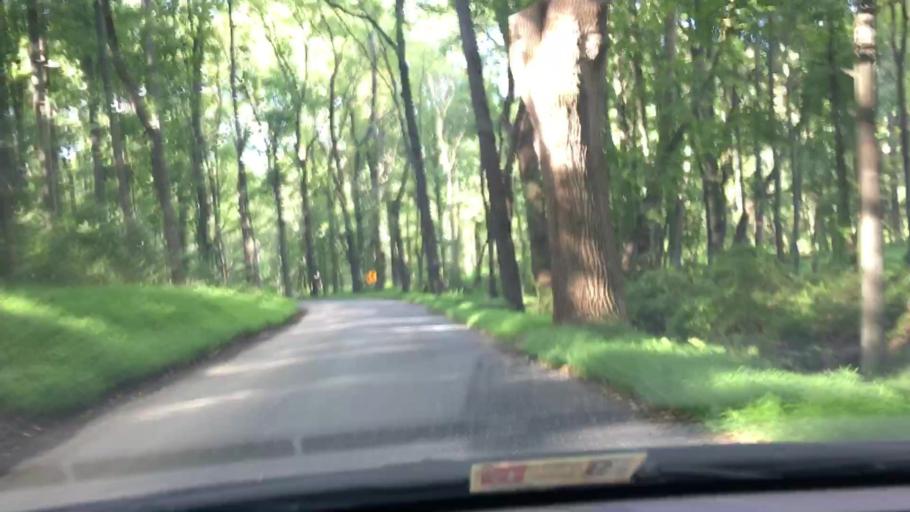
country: US
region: Maryland
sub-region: Montgomery County
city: Montgomery Village
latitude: 39.2118
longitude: -77.2049
